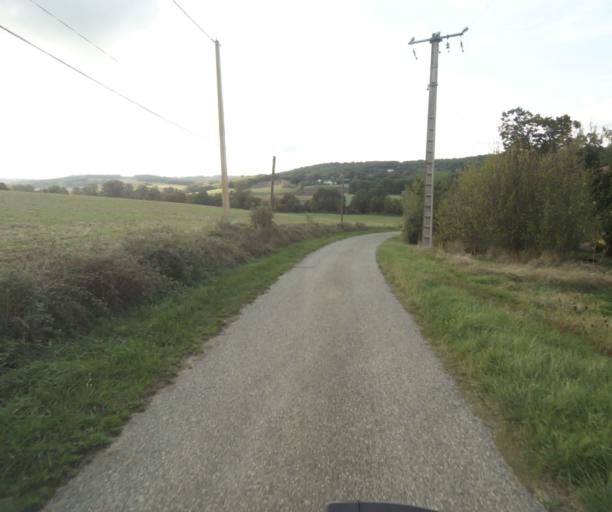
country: FR
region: Midi-Pyrenees
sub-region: Departement de la Haute-Garonne
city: Launac
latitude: 43.8070
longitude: 1.1182
